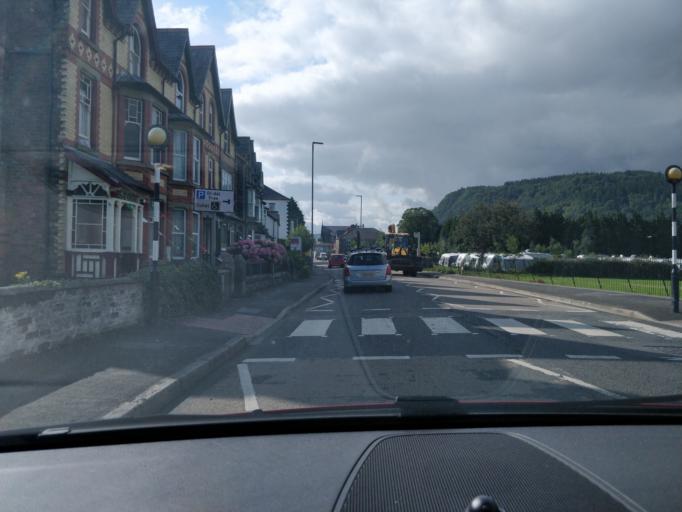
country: GB
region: Wales
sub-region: Conwy
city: Llanrwst
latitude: 53.1419
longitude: -3.8012
